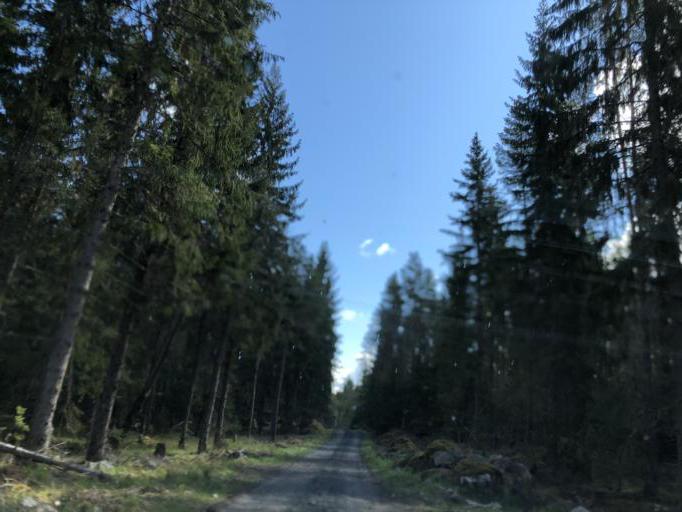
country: SE
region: Uppsala
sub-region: Heby Kommun
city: Tarnsjo
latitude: 60.2333
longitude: 16.7113
